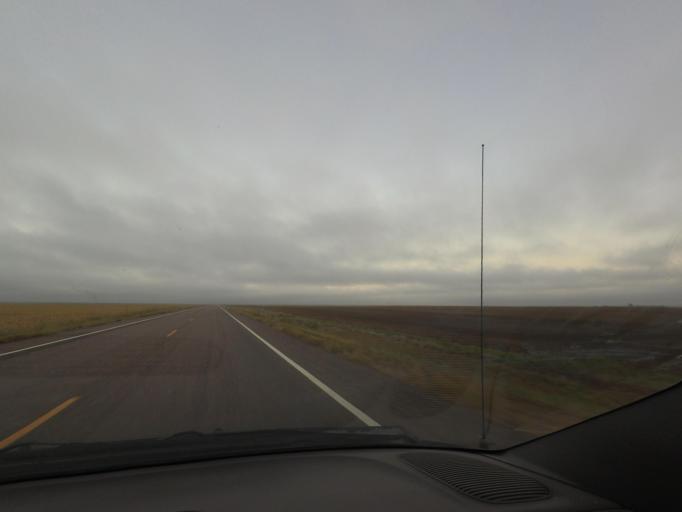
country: US
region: Kansas
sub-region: Cheyenne County
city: Saint Francis
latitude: 39.7464
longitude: -102.0981
